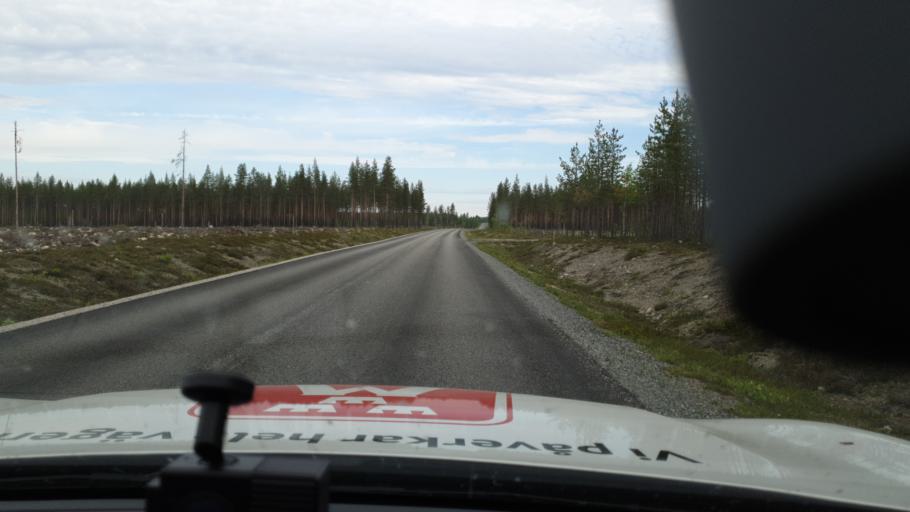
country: SE
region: Vaesterbotten
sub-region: Mala Kommun
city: Mala
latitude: 64.9546
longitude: 18.5939
